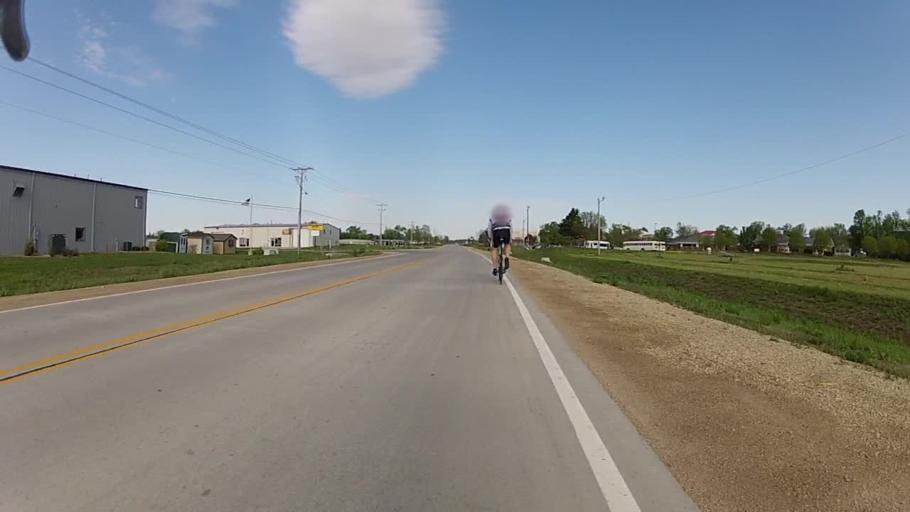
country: US
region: Kansas
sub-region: Riley County
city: Ogden
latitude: 39.1530
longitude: -96.6502
